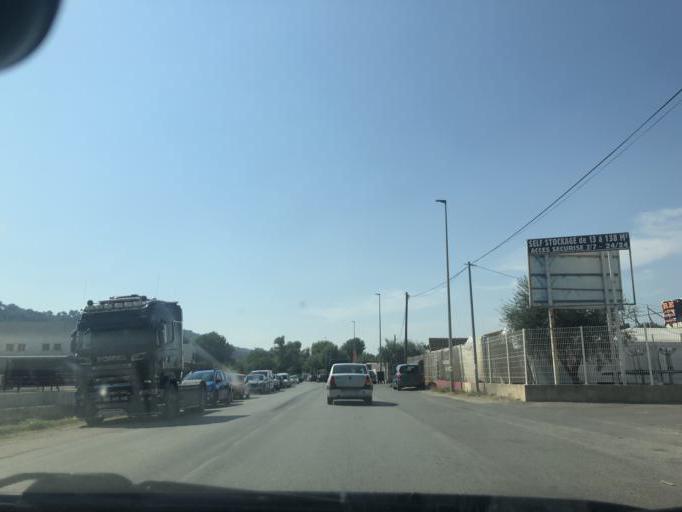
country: FR
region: Provence-Alpes-Cote d'Azur
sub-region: Departement des Alpes-Maritimes
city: Colomars
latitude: 43.7715
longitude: 7.2043
